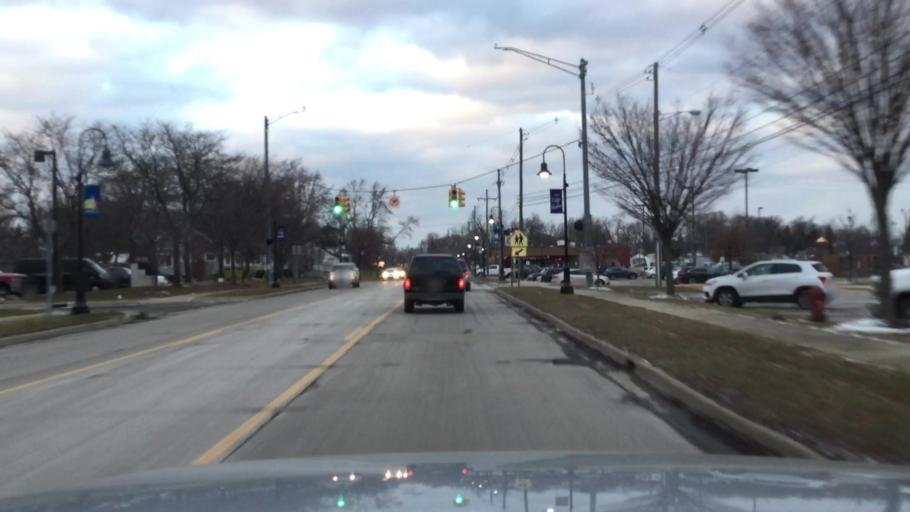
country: US
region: Michigan
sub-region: Oakland County
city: Keego Harbor
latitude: 42.6083
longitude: -83.3439
